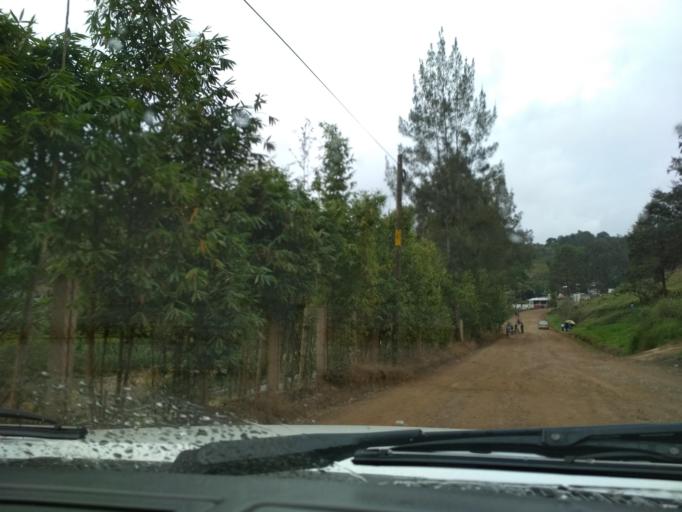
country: MX
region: Veracruz
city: El Castillo
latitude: 19.5403
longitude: -96.8317
